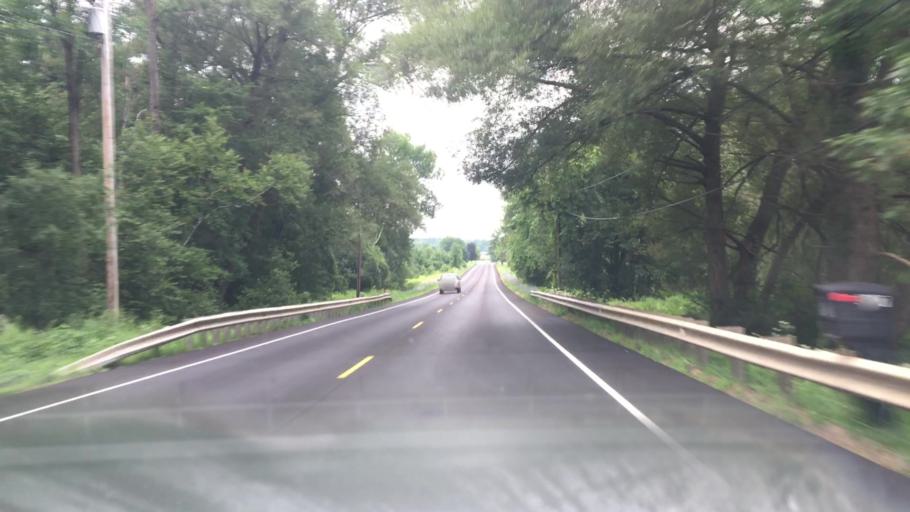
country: US
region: New York
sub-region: Clinton County
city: Morrisonville
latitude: 44.6490
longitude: -73.5599
